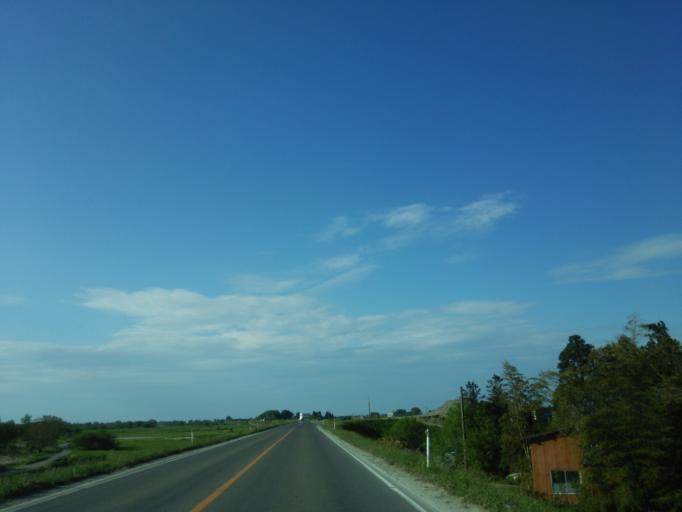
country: JP
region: Niigata
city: Gosen
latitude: 37.7912
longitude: 139.1840
